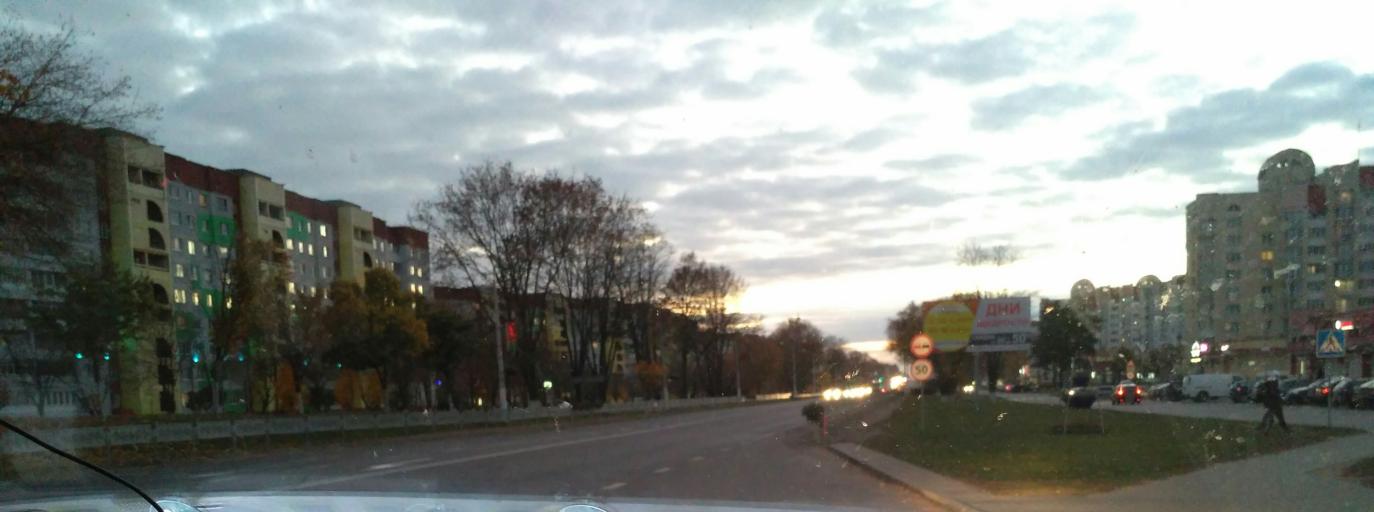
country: BY
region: Minsk
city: Horad Zhodzina
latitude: 54.0975
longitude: 28.2998
